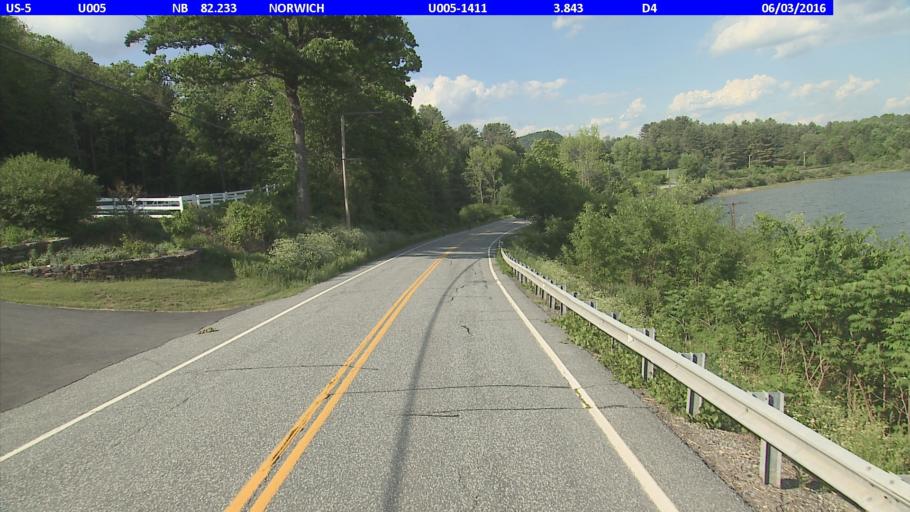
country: US
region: New Hampshire
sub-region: Grafton County
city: Hanover
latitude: 43.7333
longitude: -72.2727
